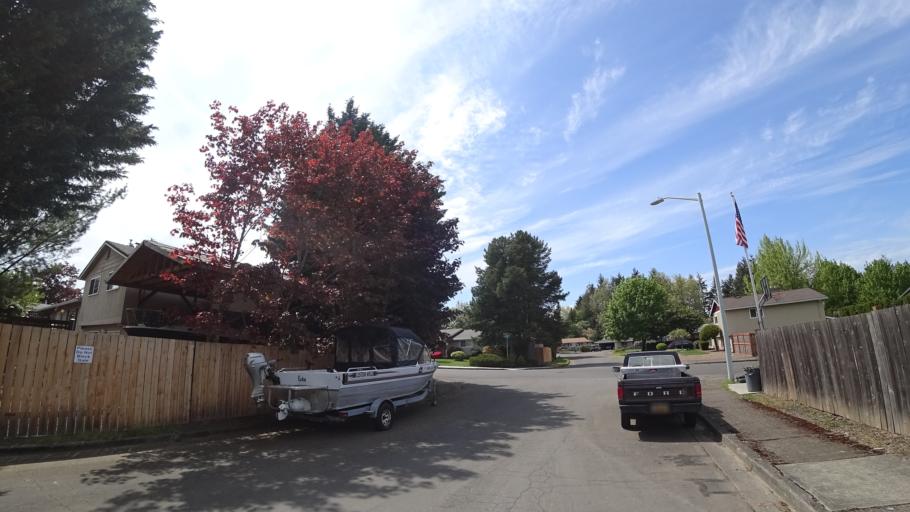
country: US
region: Oregon
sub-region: Washington County
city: Aloha
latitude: 45.4824
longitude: -122.8867
